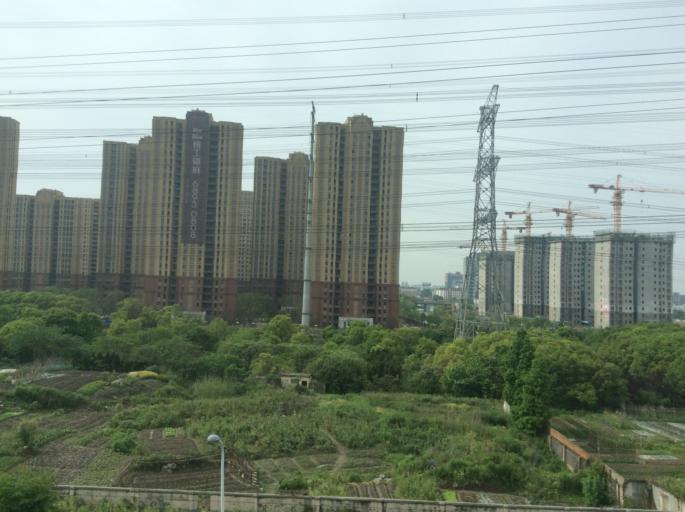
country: CN
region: Shanghai Shi
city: Kangqiao
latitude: 31.1652
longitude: 121.5617
